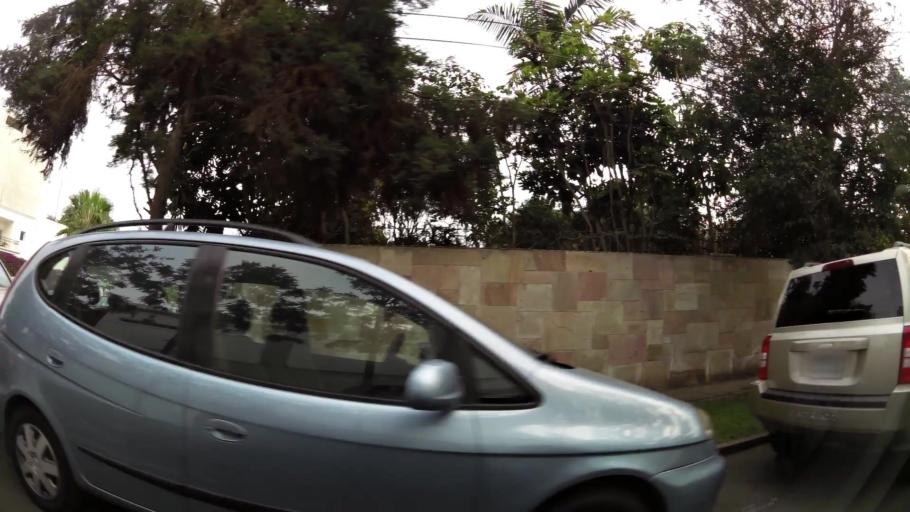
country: PE
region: Lima
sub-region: Lima
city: San Isidro
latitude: -12.1063
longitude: -77.0424
